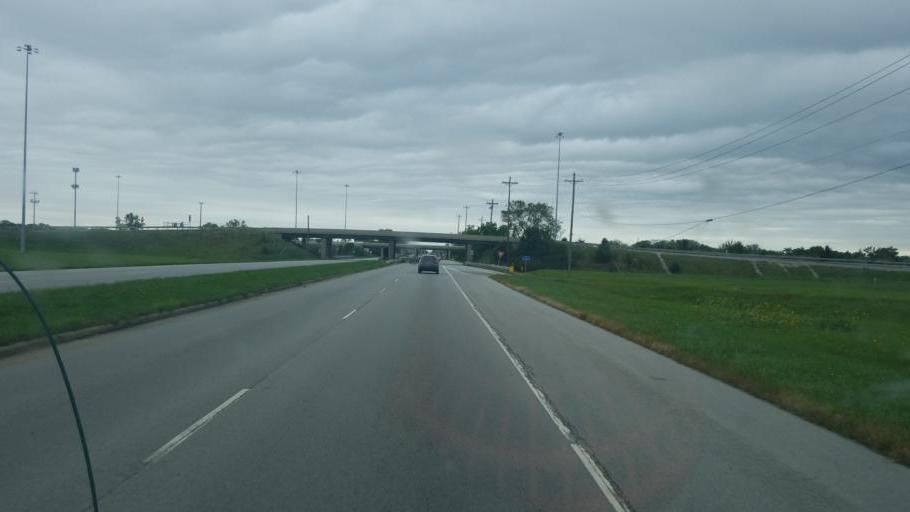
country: US
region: Ohio
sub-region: Lucas County
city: Maumee
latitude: 41.5887
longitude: -83.6647
